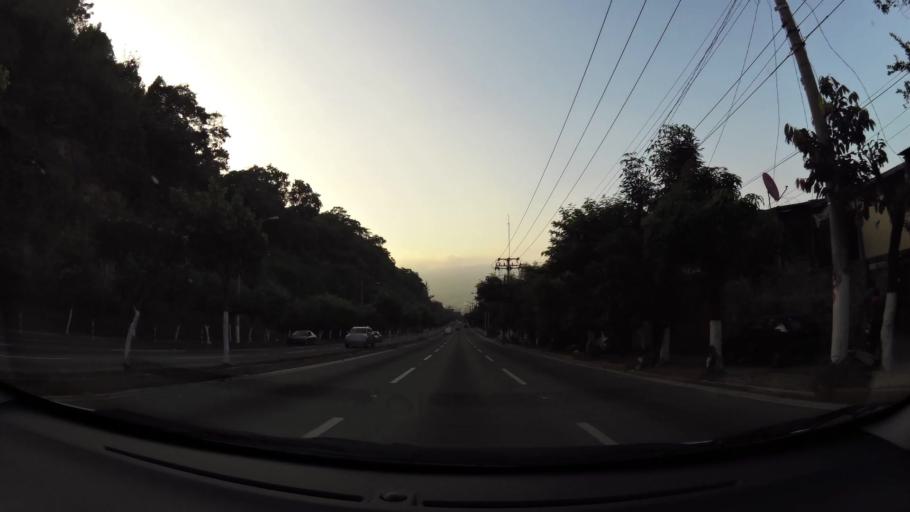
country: SV
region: San Salvador
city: San Salvador
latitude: 13.6801
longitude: -89.2138
